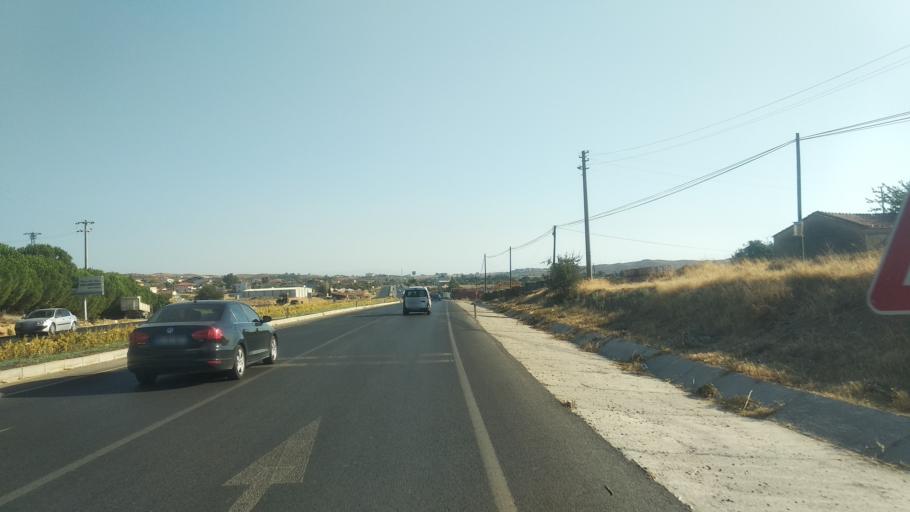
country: TR
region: Izmir
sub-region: Seferihisar
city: Seferhisar
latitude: 38.2559
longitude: 26.8324
